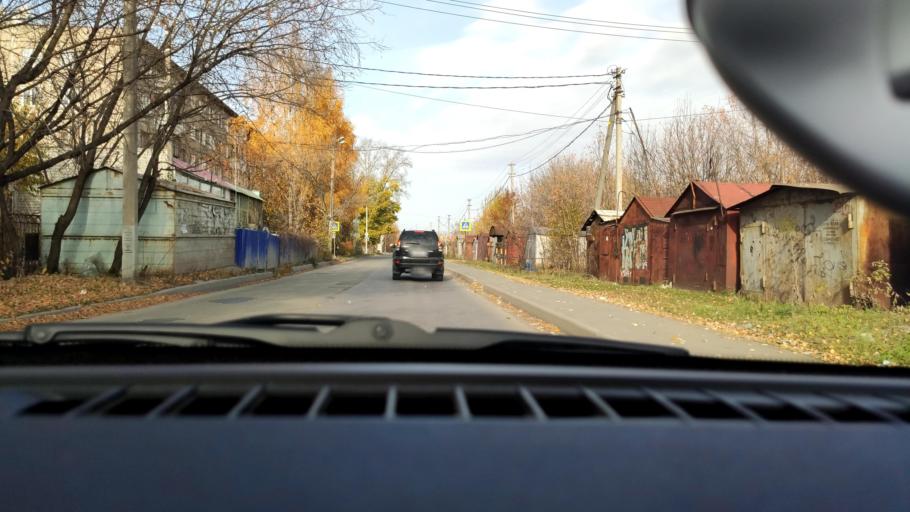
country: RU
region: Perm
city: Kondratovo
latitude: 57.9507
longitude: 56.1174
